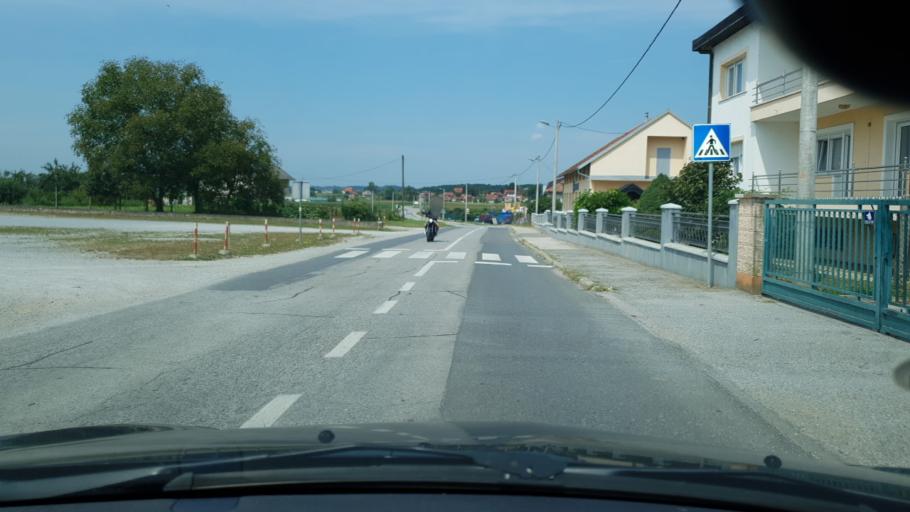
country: HR
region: Krapinsko-Zagorska
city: Zlatar
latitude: 46.0525
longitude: 16.0788
